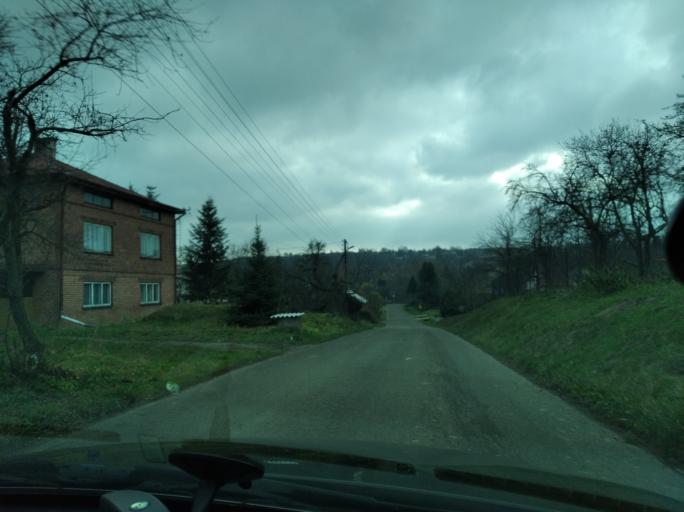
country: PL
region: Subcarpathian Voivodeship
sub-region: Powiat przeworski
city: Sietesz
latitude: 49.9828
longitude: 22.3450
